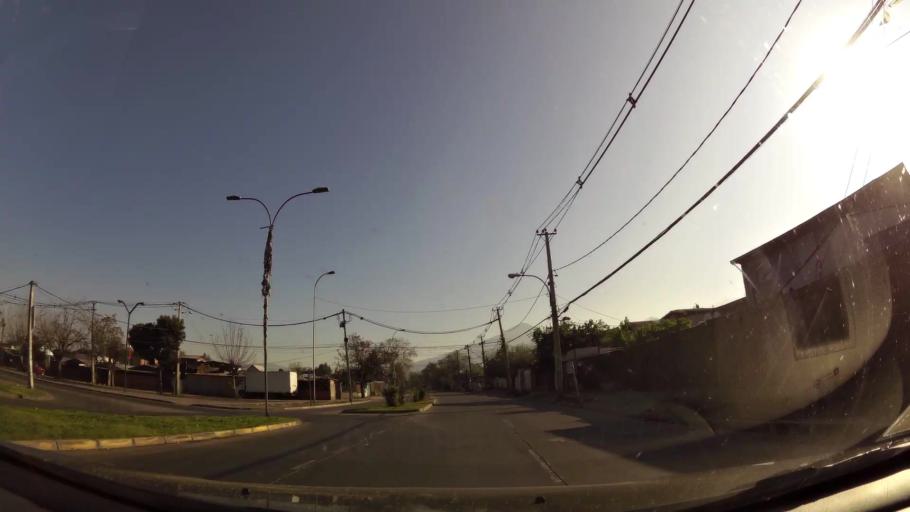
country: CL
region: Santiago Metropolitan
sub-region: Provincia de Santiago
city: Santiago
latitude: -33.3935
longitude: -70.6573
